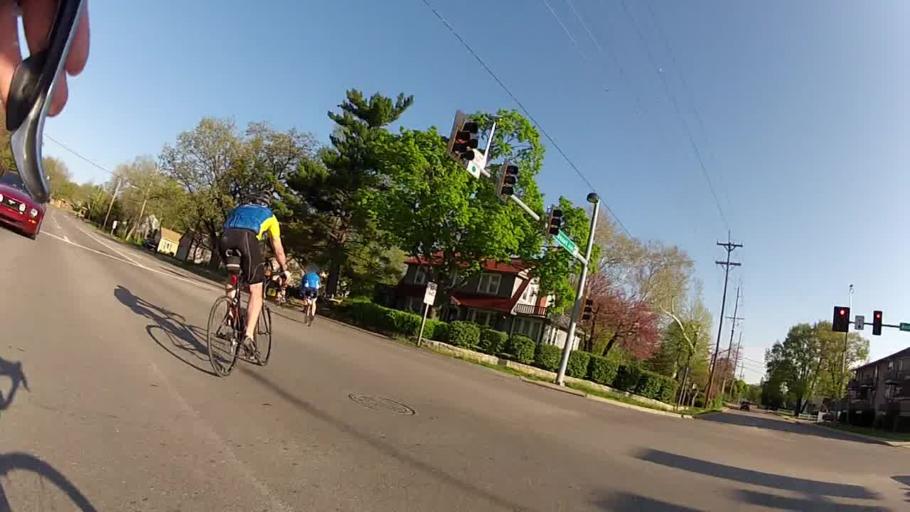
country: US
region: Kansas
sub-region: Riley County
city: Manhattan
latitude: 39.1859
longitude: -96.5889
